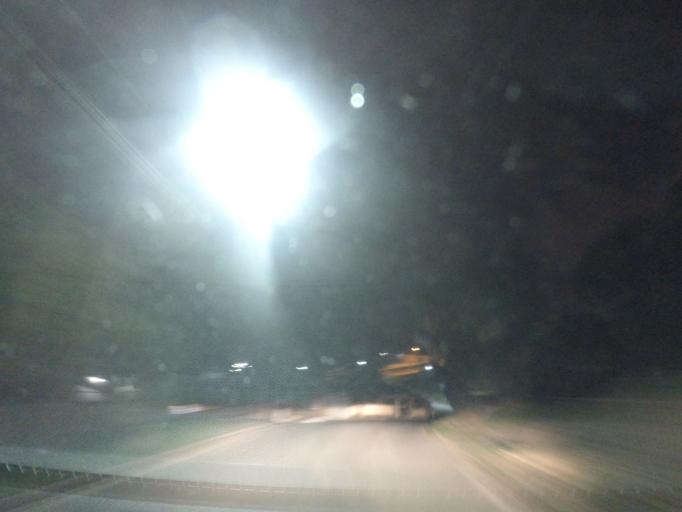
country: BR
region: Parana
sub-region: Almirante Tamandare
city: Almirante Tamandare
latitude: -25.3674
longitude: -49.2815
